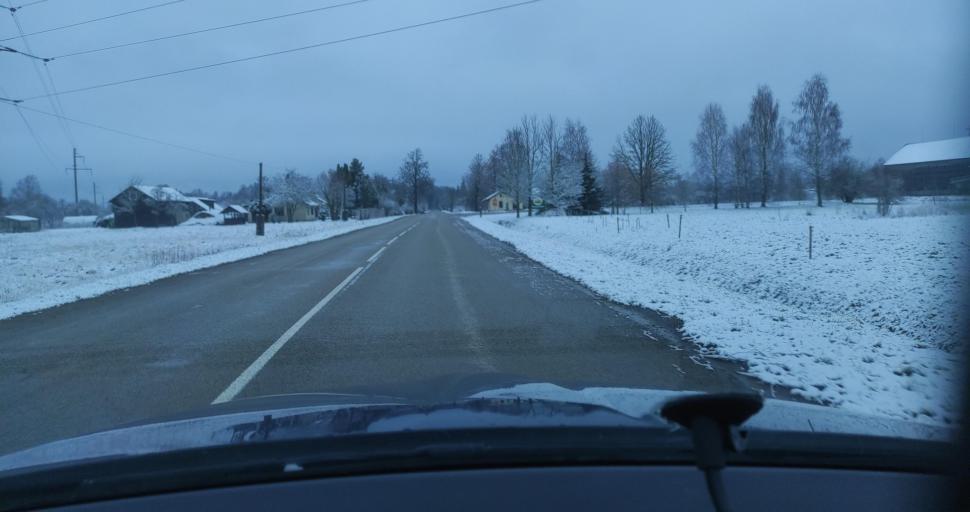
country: LV
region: Skrunda
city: Skrunda
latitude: 56.8671
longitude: 22.2322
